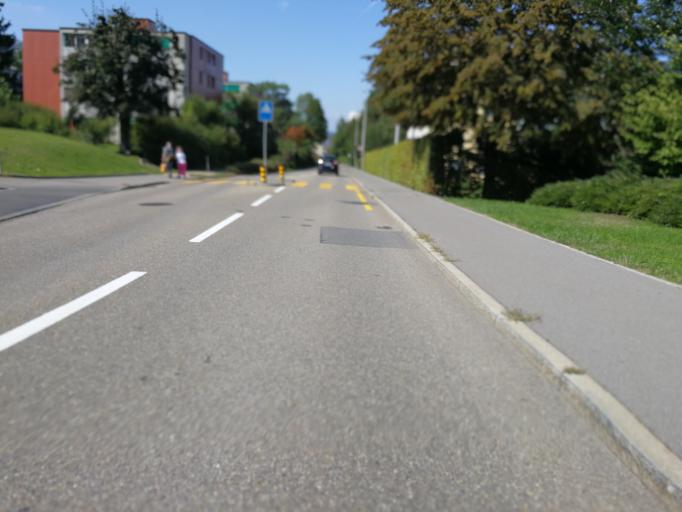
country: CH
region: Zurich
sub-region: Bezirk Horgen
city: Horgen
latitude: 47.2531
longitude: 8.6000
